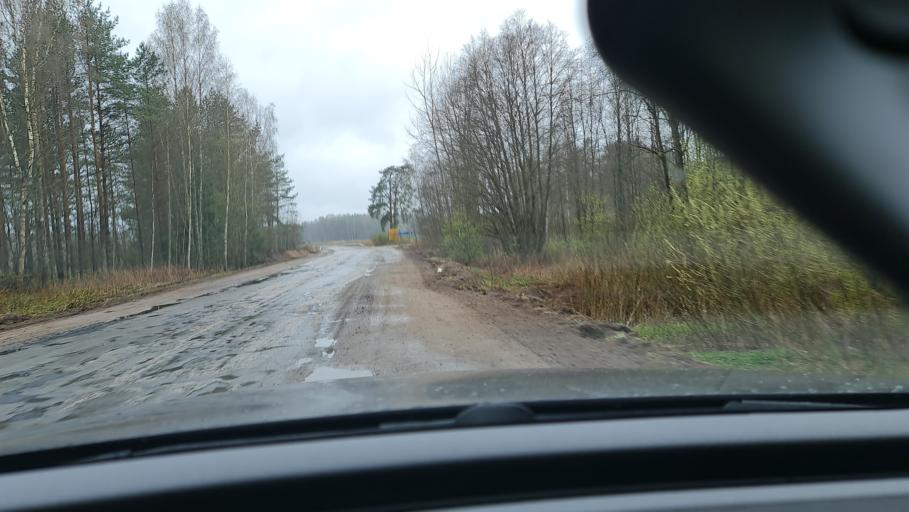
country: RU
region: Novgorod
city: Valday
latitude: 58.0407
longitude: 32.9104
